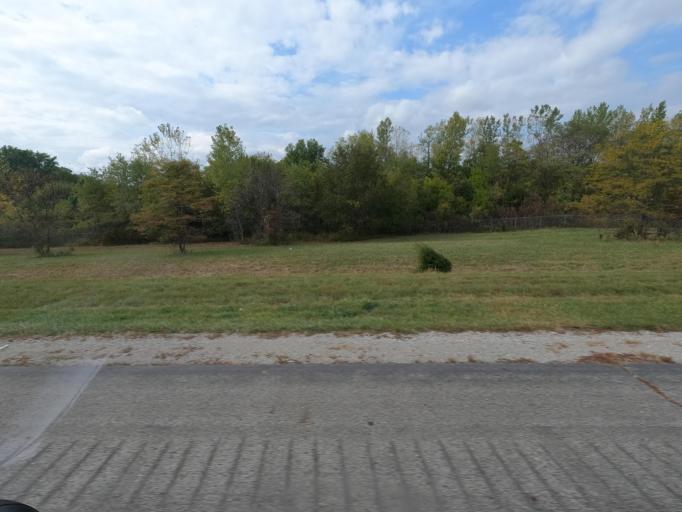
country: US
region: Iowa
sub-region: Polk County
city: Pleasant Hill
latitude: 41.6105
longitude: -93.4952
